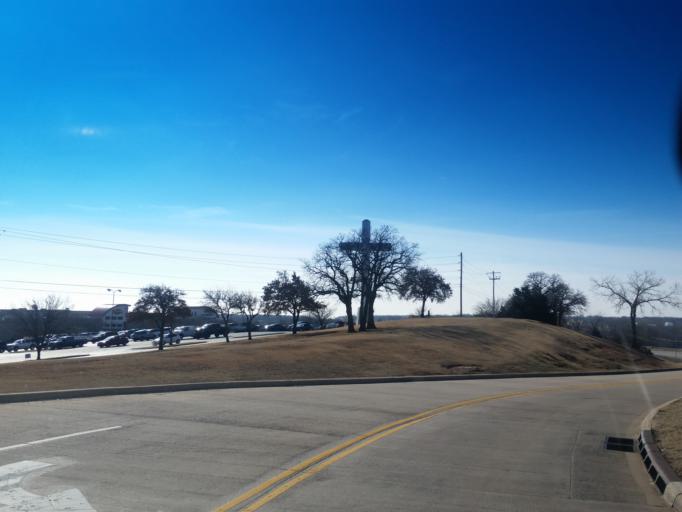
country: US
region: Oklahoma
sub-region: Oklahoma County
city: Edmond
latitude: 35.6521
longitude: -97.4220
